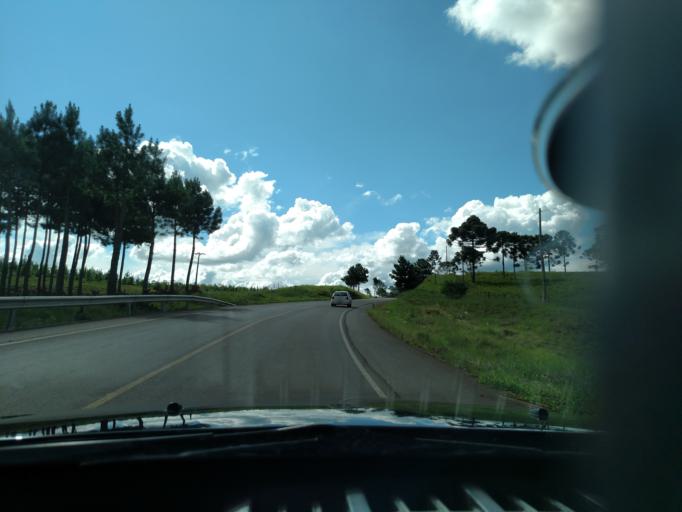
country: BR
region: Rio Grande do Sul
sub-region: Vacaria
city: Estrela
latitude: -27.9200
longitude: -50.7003
